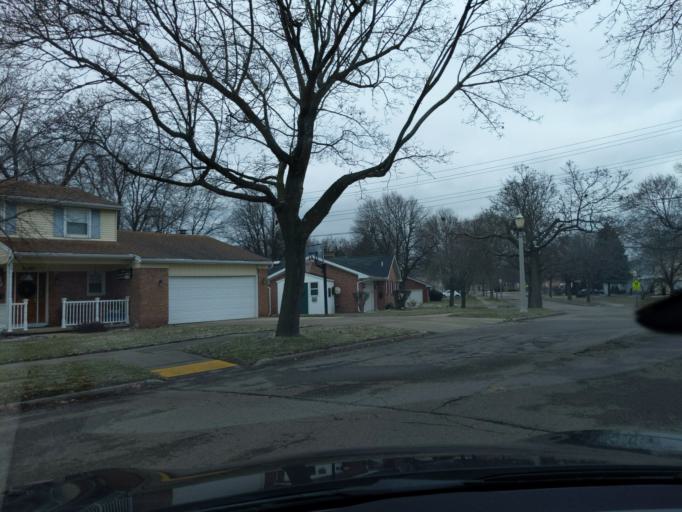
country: US
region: Michigan
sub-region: Ingham County
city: East Lansing
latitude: 42.7561
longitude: -84.5164
